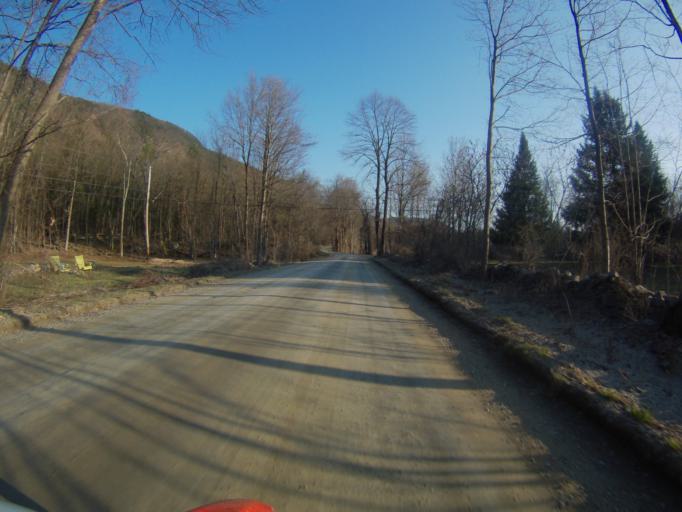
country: US
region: Vermont
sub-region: Addison County
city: Bristol
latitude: 44.1058
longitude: -73.0756
